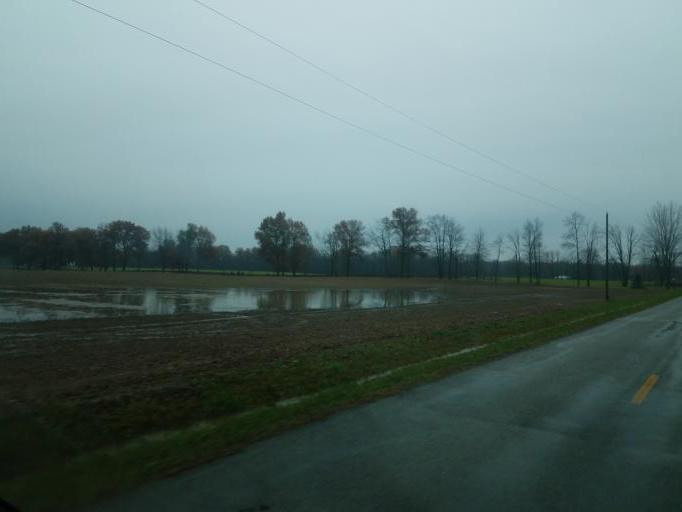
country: US
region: Ohio
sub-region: Delaware County
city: Sunbury
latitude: 40.3040
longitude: -82.7964
